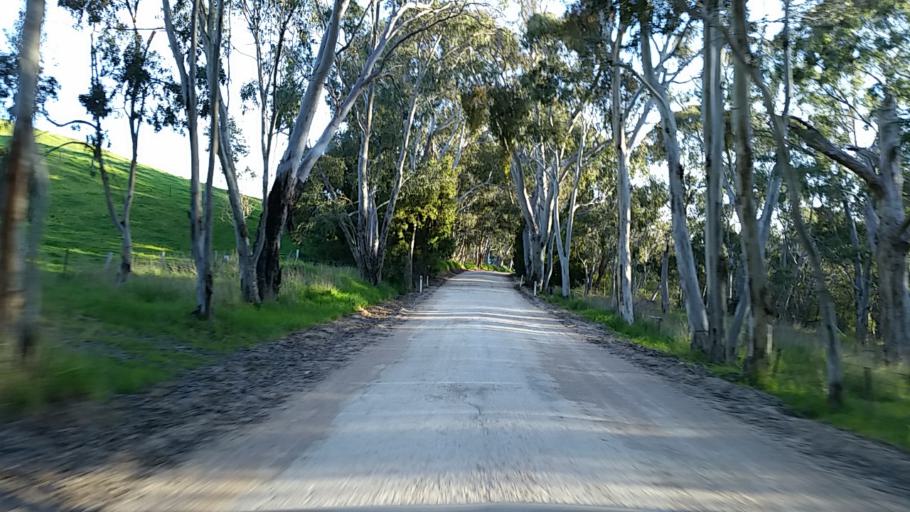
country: AU
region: South Australia
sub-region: Alexandrina
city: Mount Compass
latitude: -35.2766
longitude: 138.7011
